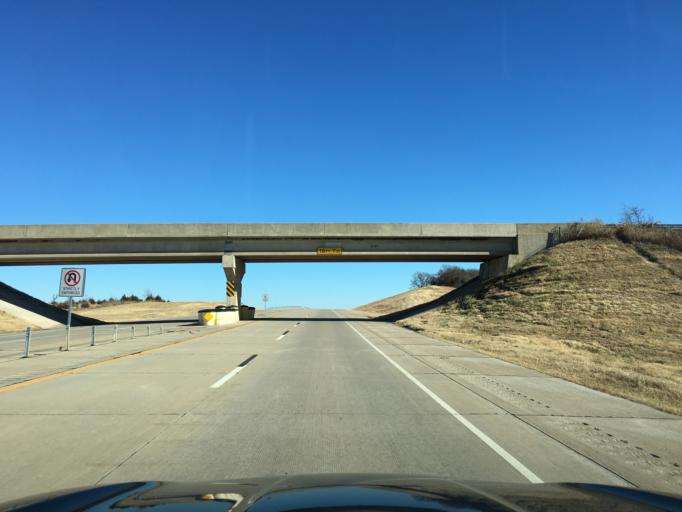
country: US
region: Oklahoma
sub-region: Payne County
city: Yale
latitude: 36.2251
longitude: -96.6433
